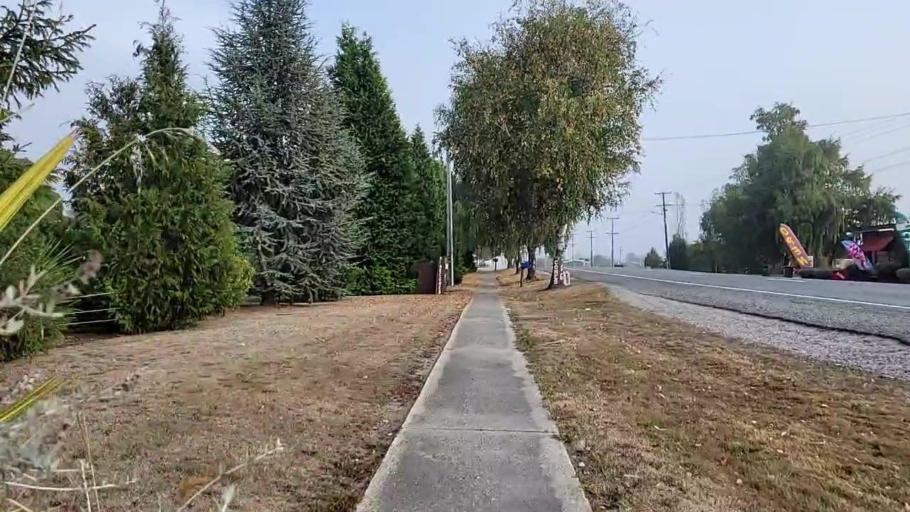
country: NZ
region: Southland
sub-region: Gore District
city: Gore
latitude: -45.6343
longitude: 169.3635
